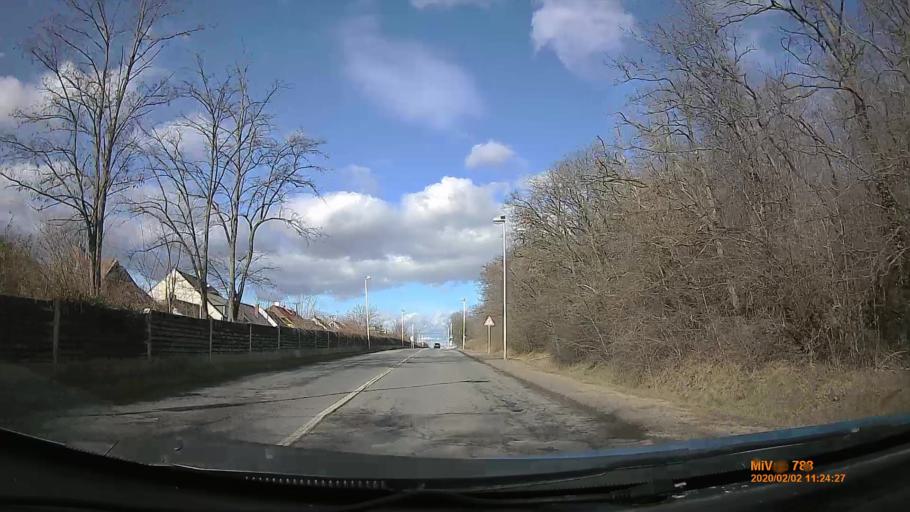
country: HU
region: Gyor-Moson-Sopron
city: Sopron
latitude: 47.6956
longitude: 16.5839
